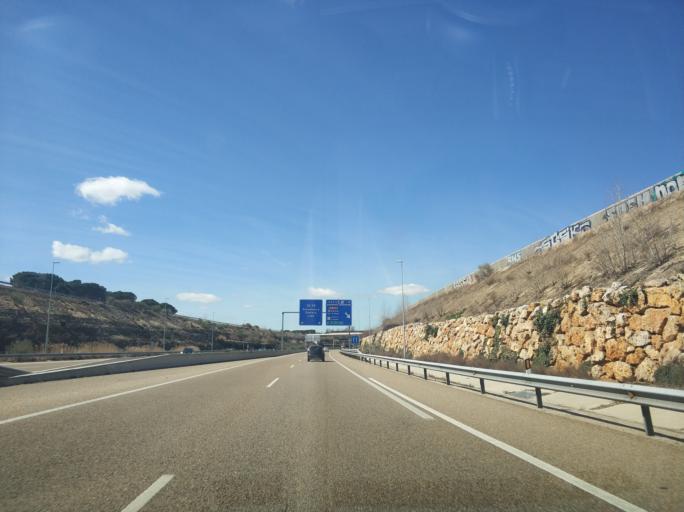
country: ES
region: Castille and Leon
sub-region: Provincia de Valladolid
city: Laguna de Duero
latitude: 41.6066
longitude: -4.7330
